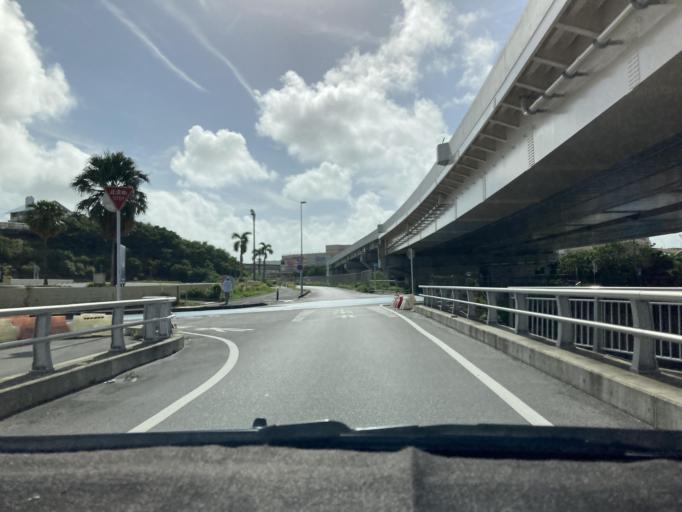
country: JP
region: Okinawa
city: Naha-shi
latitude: 26.2034
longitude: 127.7353
